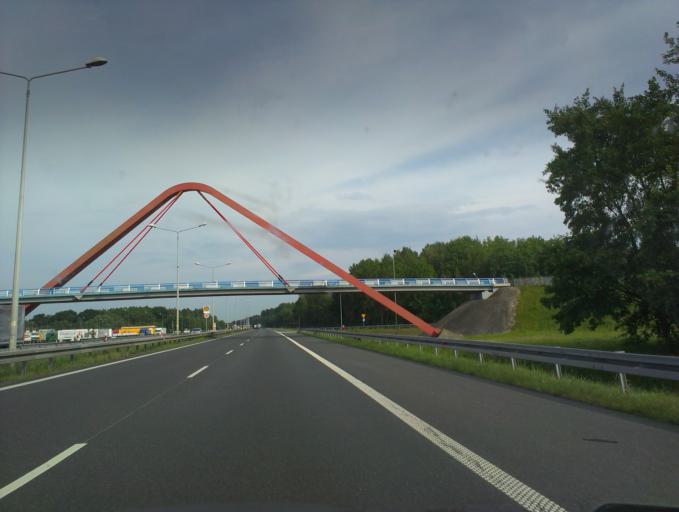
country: PL
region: Opole Voivodeship
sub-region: Powiat opolski
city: Niemodlin
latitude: 50.6776
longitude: 17.6525
